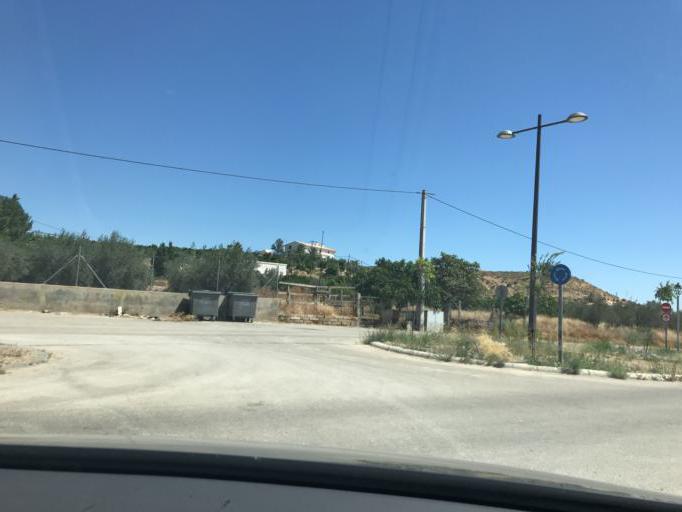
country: ES
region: Andalusia
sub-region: Provincia de Almeria
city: Fines
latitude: 37.3562
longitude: -2.2533
